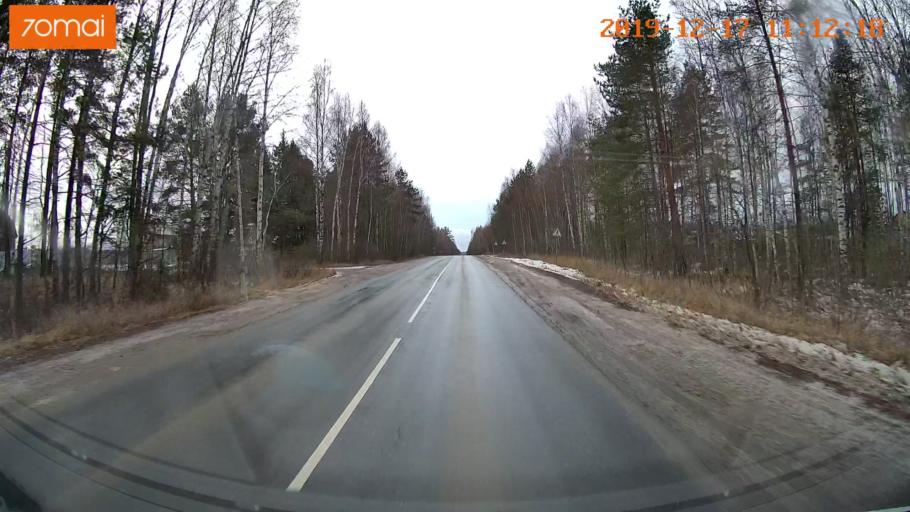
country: RU
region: Vladimir
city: Gus'-Khrustal'nyy
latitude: 55.5776
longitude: 40.6298
